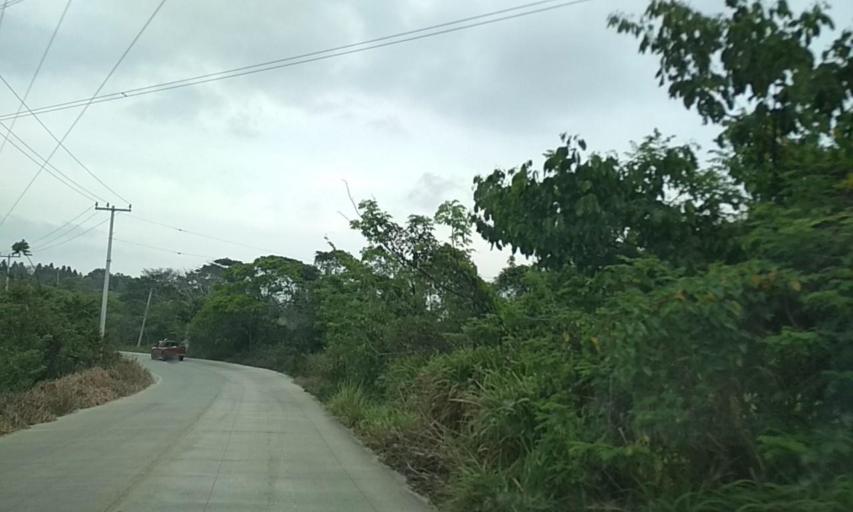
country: MX
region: Veracruz
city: Las Choapas
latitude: 17.7975
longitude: -94.1104
